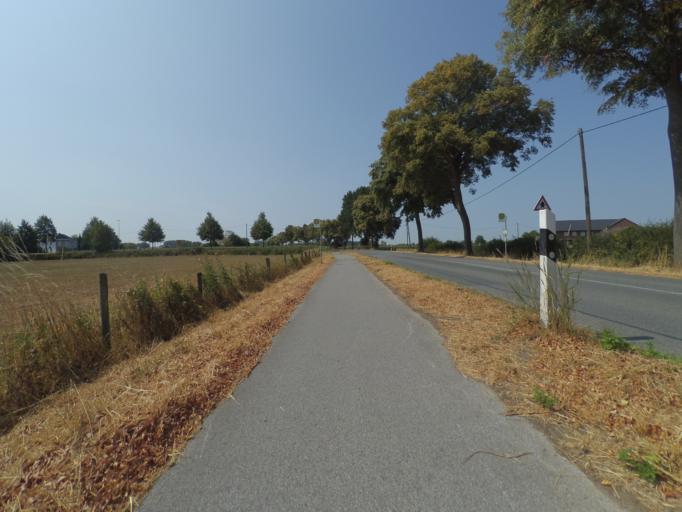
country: DE
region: North Rhine-Westphalia
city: Rees
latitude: 51.7943
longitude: 6.4137
